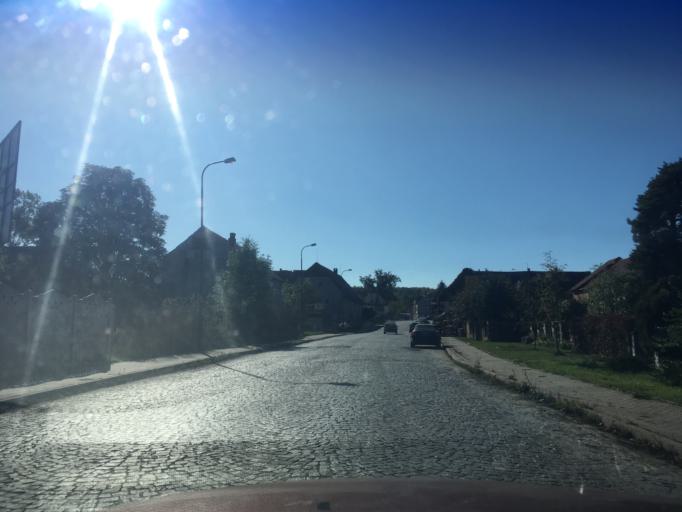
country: DE
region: Saxony
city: Zittau
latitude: 50.8978
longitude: 14.8442
